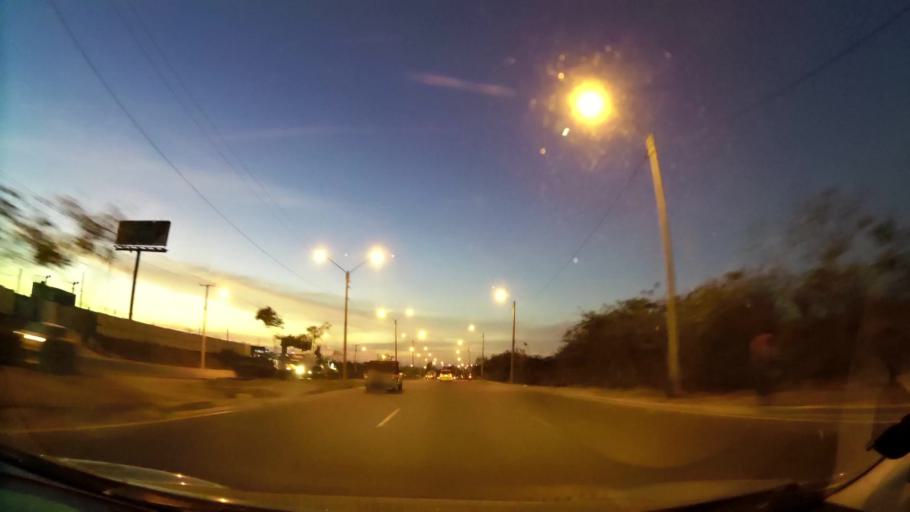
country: CO
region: Atlantico
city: Barranquilla
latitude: 10.9286
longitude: -74.8288
